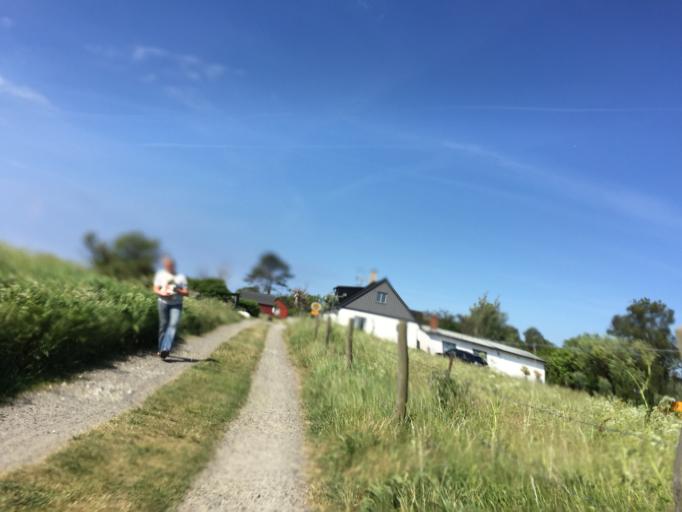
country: SE
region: Skane
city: Smygehamn
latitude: 55.3427
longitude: 13.3213
